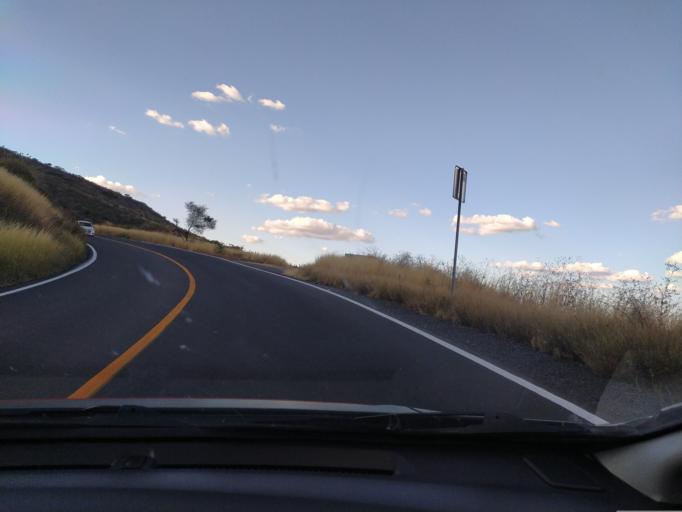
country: MX
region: Guanajuato
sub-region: Purisima del Rincon
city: Monte Grande
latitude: 21.0216
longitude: -101.8963
